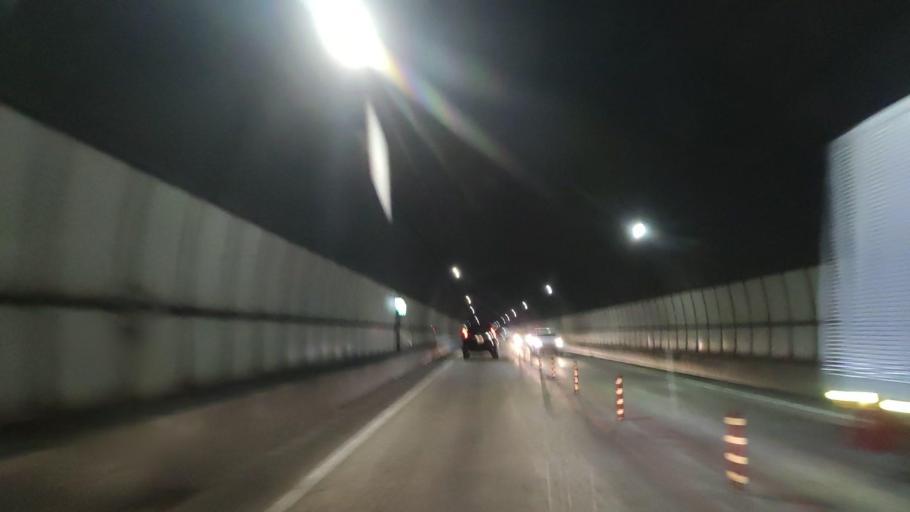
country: JP
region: Yamagata
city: Shinjo
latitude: 38.6855
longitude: 140.3152
